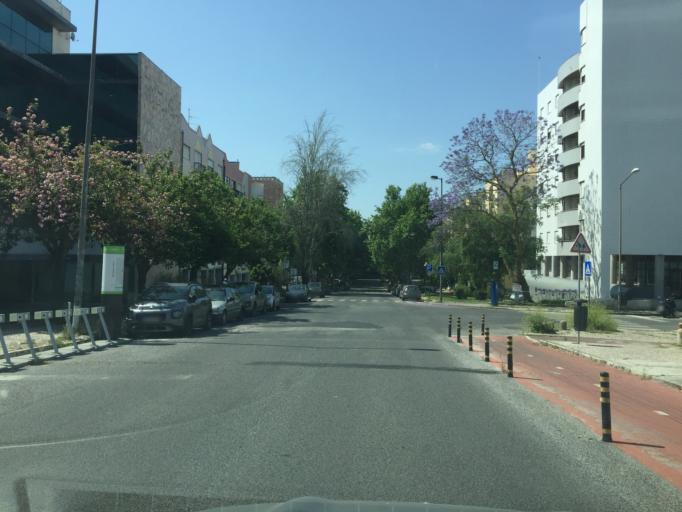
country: PT
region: Lisbon
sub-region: Odivelas
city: Pontinha
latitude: 38.7597
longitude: -9.1700
